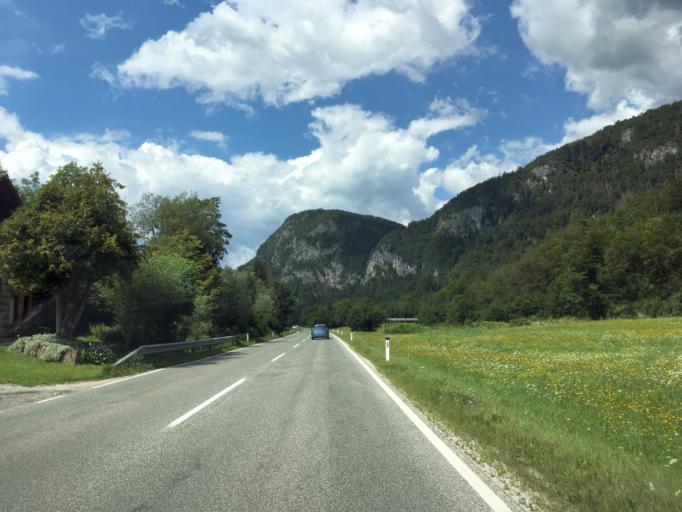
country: SI
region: Bohinj
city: Bohinjska Bistrica
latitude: 46.2888
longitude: 13.9932
